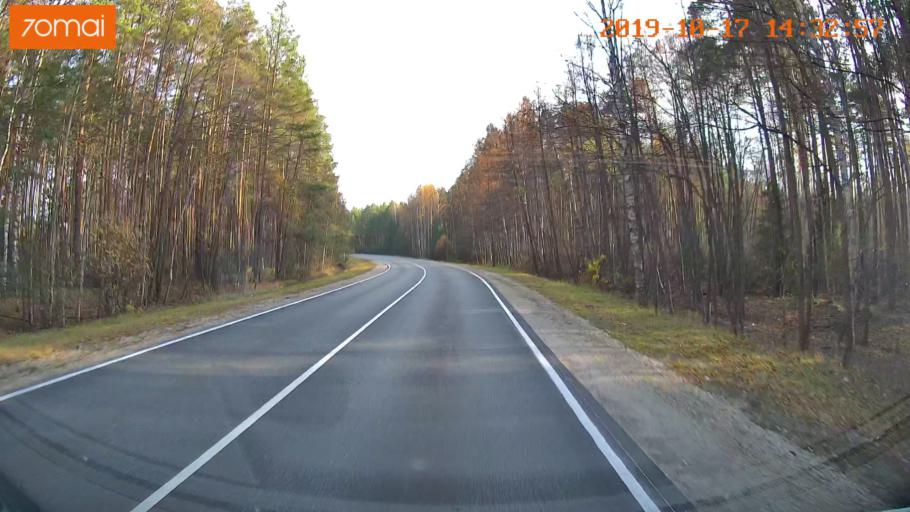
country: RU
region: Rjazan
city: Solotcha
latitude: 54.9260
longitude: 39.9889
